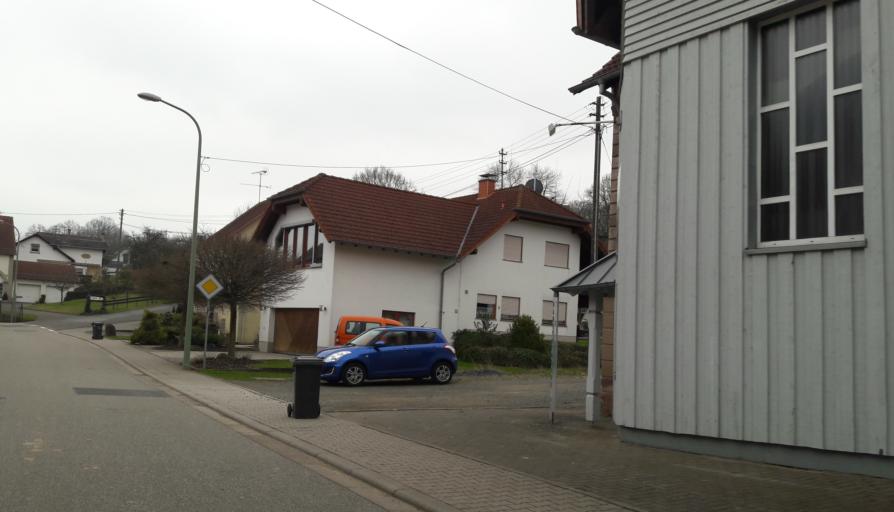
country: DE
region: Rheinland-Pfalz
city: Langenbach
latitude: 49.4948
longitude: 7.3225
